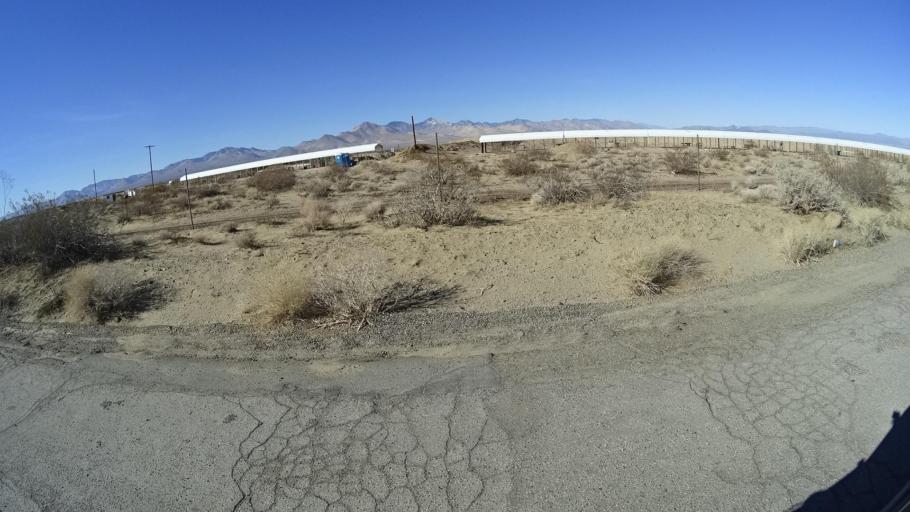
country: US
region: California
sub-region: Kern County
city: China Lake Acres
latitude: 35.5660
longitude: -117.7789
